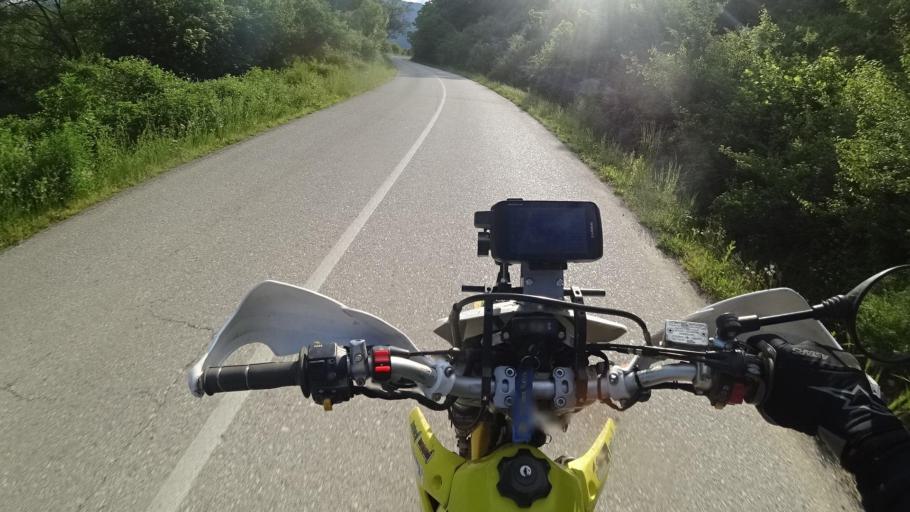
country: BA
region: Federation of Bosnia and Herzegovina
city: Sanica
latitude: 44.6194
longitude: 16.6696
